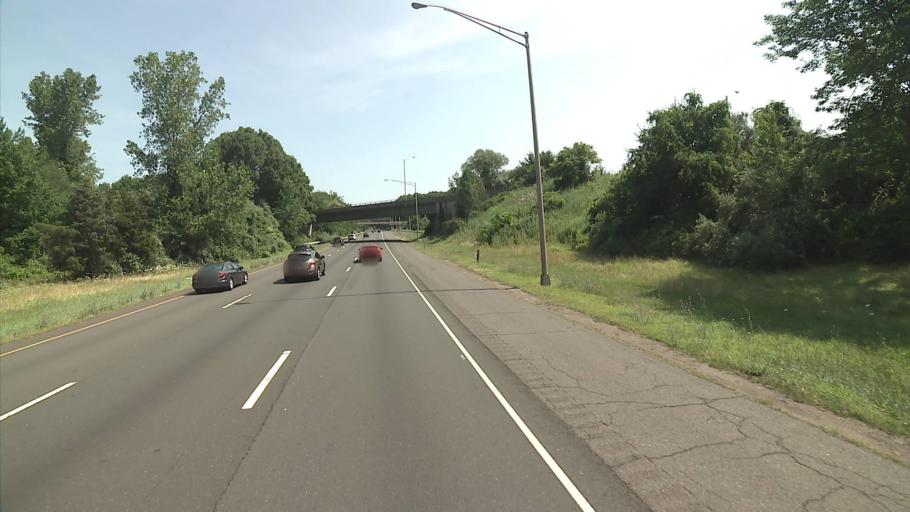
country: US
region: Connecticut
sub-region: Middlesex County
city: Cromwell
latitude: 41.6211
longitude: -72.6930
